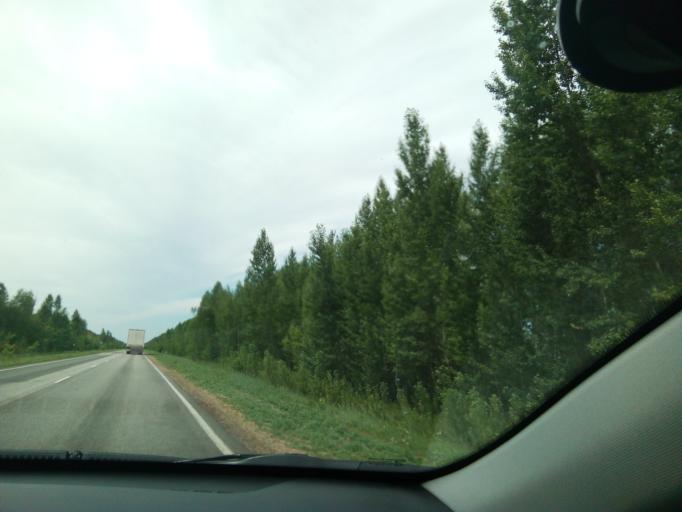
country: RU
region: Tambov
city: Zavoronezhskoye
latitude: 52.6217
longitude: 40.8417
